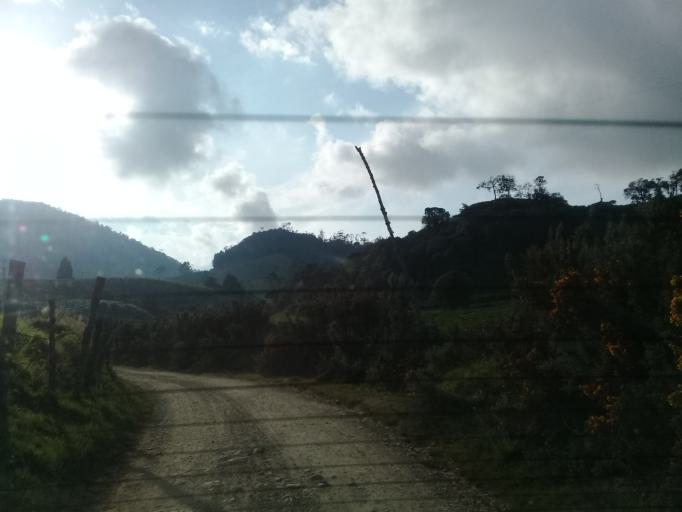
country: CO
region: Cundinamarca
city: Sibate
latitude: 4.4352
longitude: -74.2868
